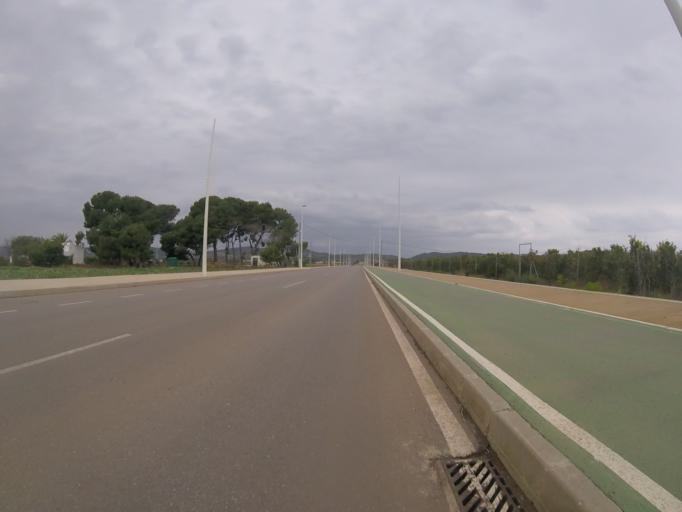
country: ES
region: Valencia
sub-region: Provincia de Castello
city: Torreblanca
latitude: 40.2210
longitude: 0.2151
